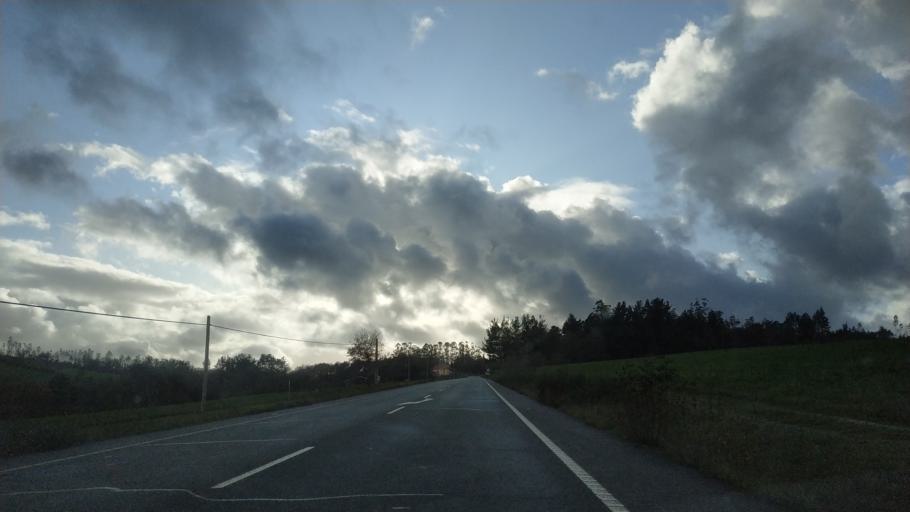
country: ES
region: Galicia
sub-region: Provincia da Coruna
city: Arzua
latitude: 42.8808
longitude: -8.1995
